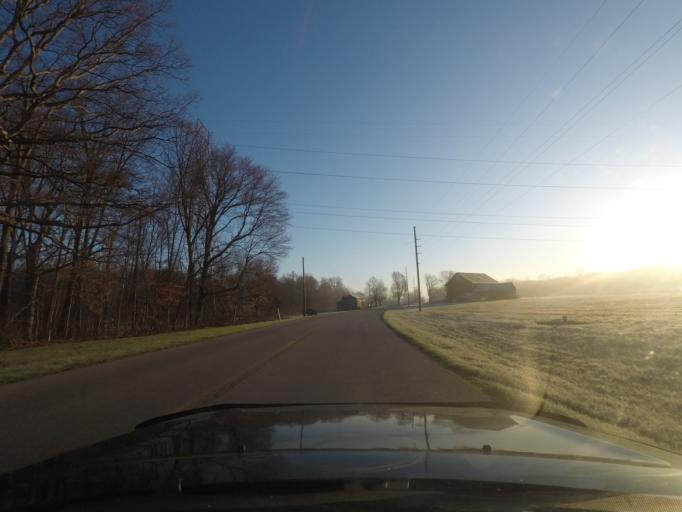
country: US
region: Indiana
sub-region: Marshall County
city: Bremen
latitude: 41.4538
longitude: -86.0938
